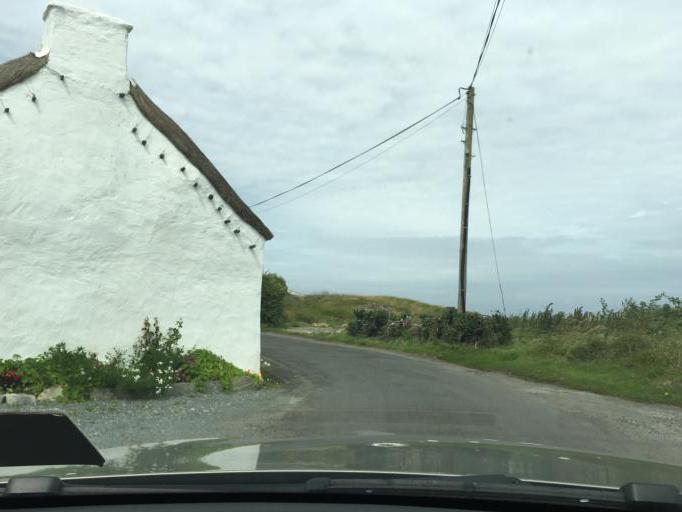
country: IE
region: Ulster
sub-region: County Donegal
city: Carndonagh
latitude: 55.3766
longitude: -7.3653
